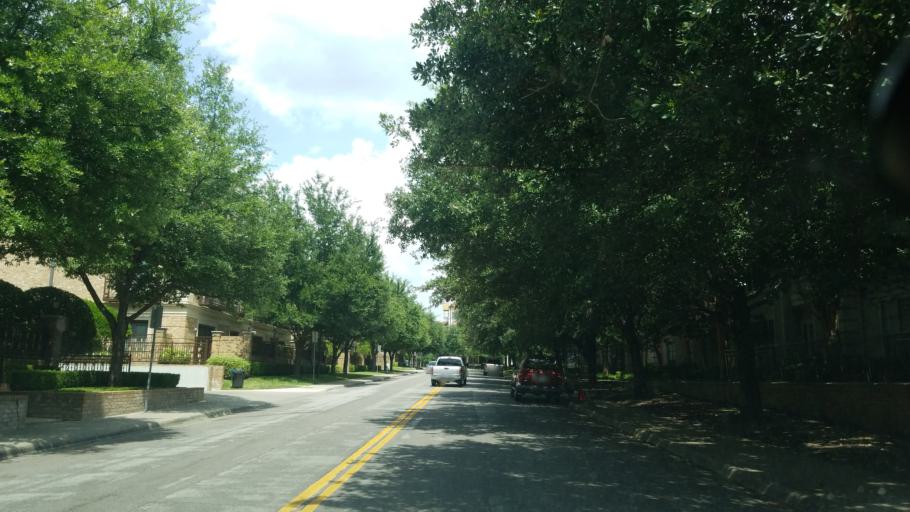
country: US
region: Texas
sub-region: Dallas County
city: University Park
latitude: 32.8677
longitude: -96.7913
